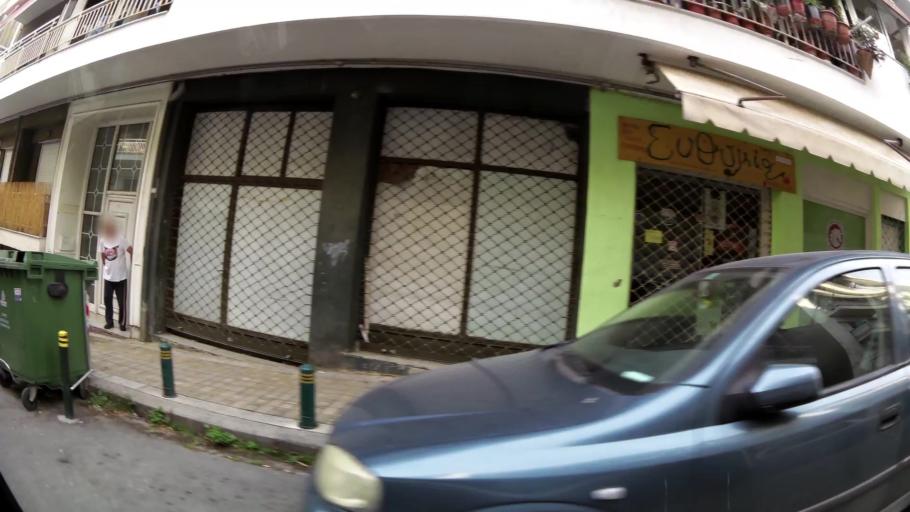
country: GR
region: Central Macedonia
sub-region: Nomos Thessalonikis
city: Ampelokipoi
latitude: 40.6553
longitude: 22.9371
